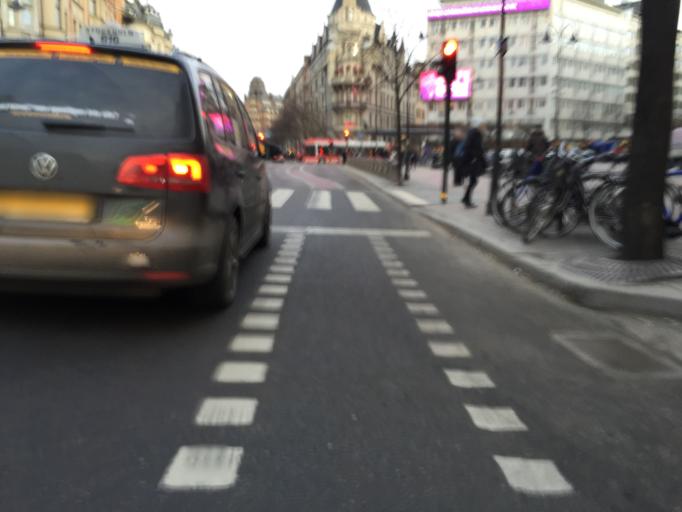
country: SE
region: Stockholm
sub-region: Stockholms Kommun
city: Stockholm
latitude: 59.3356
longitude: 18.0732
